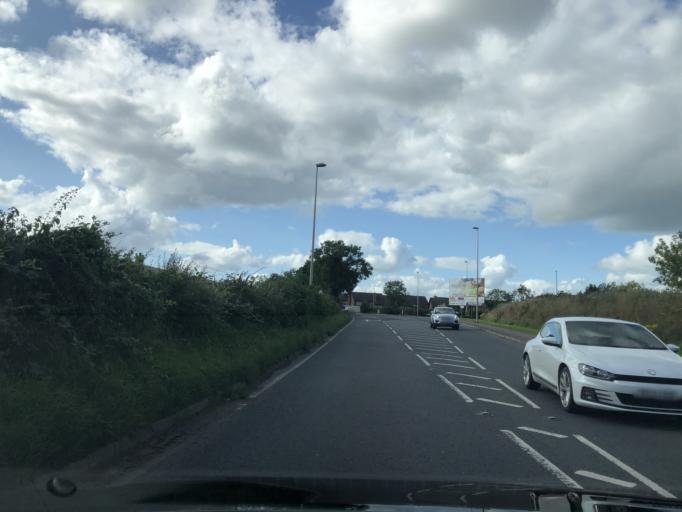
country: GB
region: Northern Ireland
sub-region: Castlereagh District
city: Dundonald
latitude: 54.5806
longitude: -5.7928
